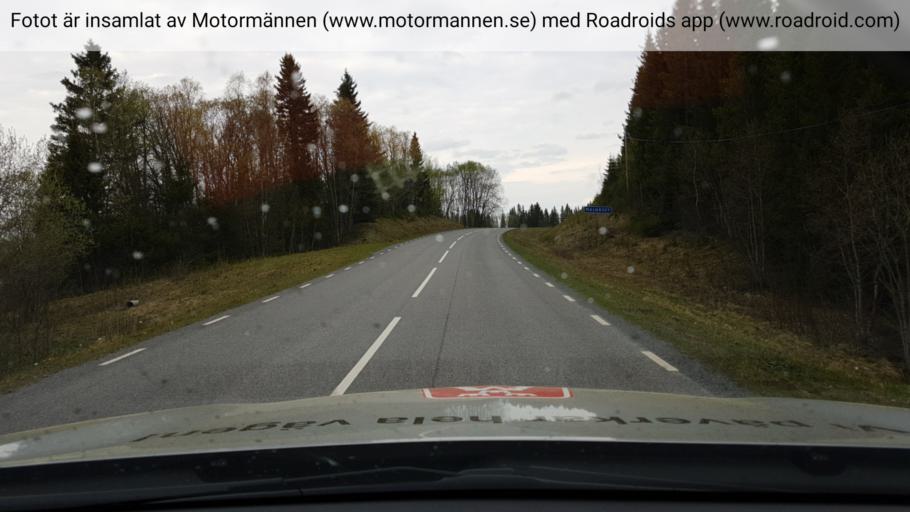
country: SE
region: Jaemtland
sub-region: Are Kommun
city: Are
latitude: 63.5822
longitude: 13.0201
